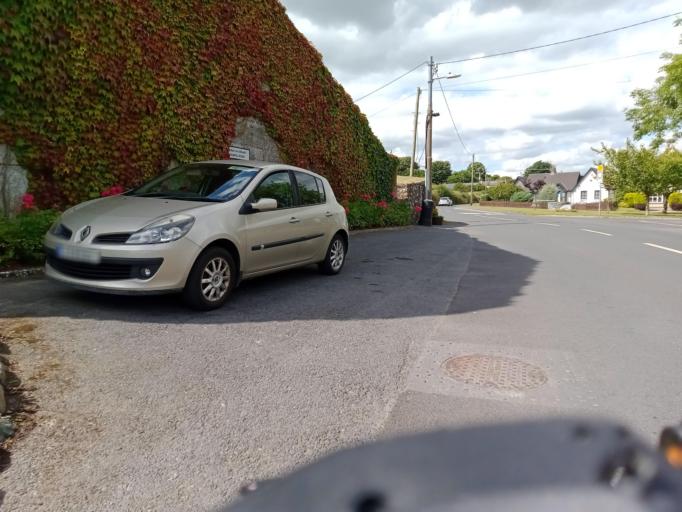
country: IE
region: Munster
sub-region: Waterford
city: Dungarvan
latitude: 52.1316
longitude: -7.4626
